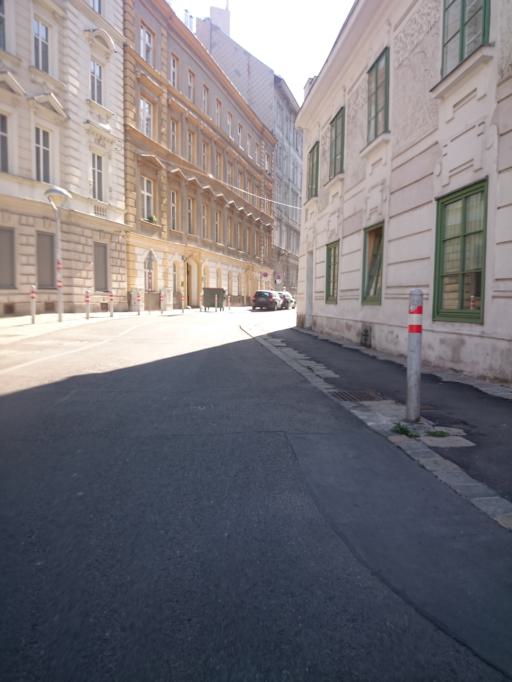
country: AT
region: Vienna
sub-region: Wien Stadt
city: Vienna
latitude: 48.2086
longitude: 16.3458
